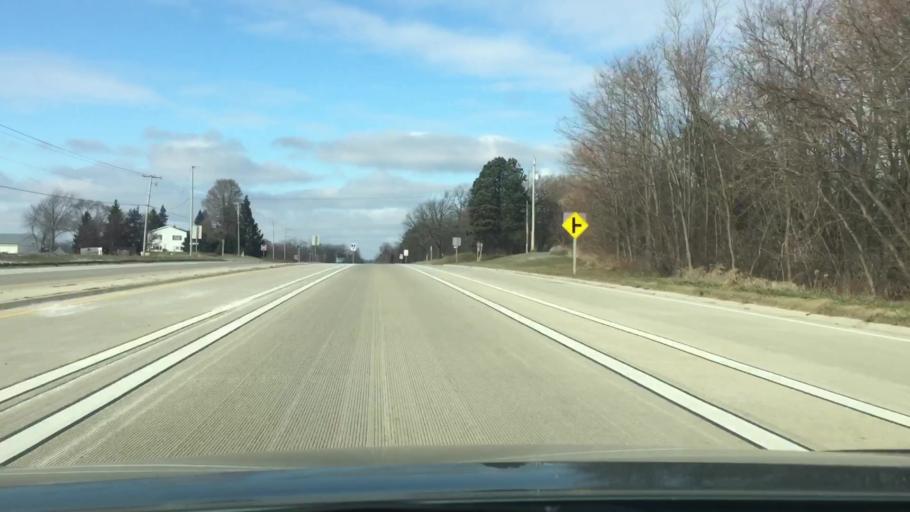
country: US
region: Wisconsin
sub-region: Waukesha County
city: North Prairie
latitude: 42.9458
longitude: -88.3502
